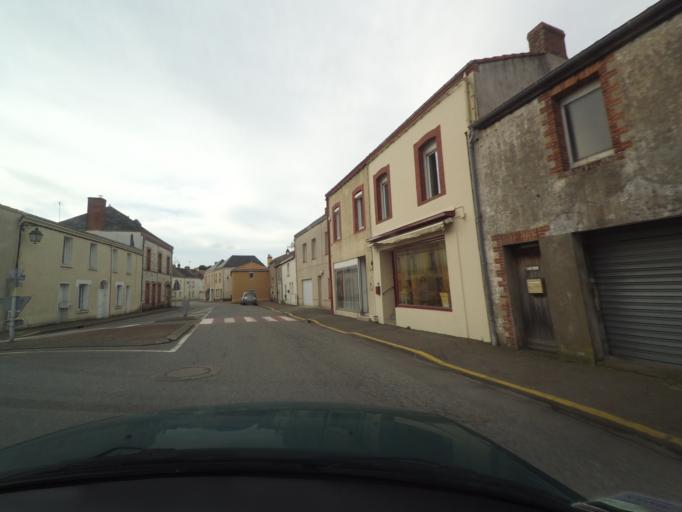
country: FR
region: Pays de la Loire
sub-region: Departement de la Loire-Atlantique
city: Chauve
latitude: 47.1513
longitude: -1.9854
